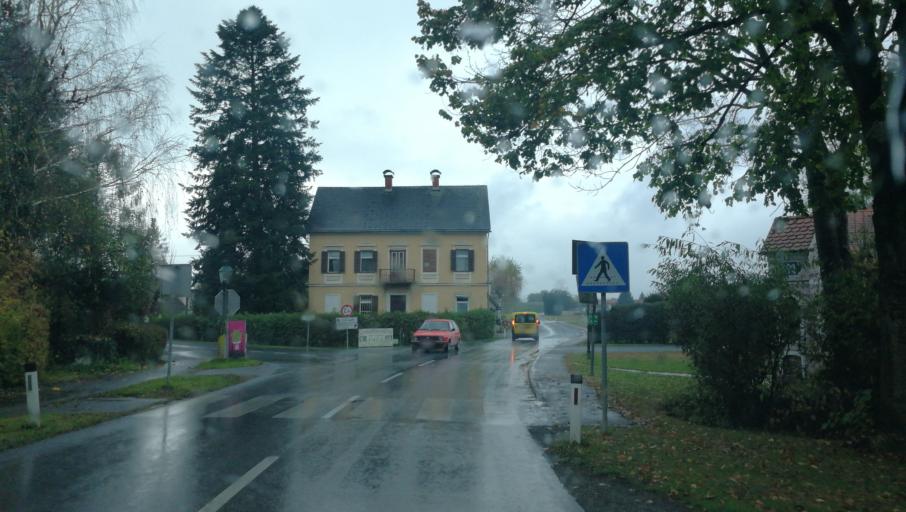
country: AT
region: Styria
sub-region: Politischer Bezirk Leibnitz
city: Sankt Veit am Vogau
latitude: 46.7452
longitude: 15.6238
